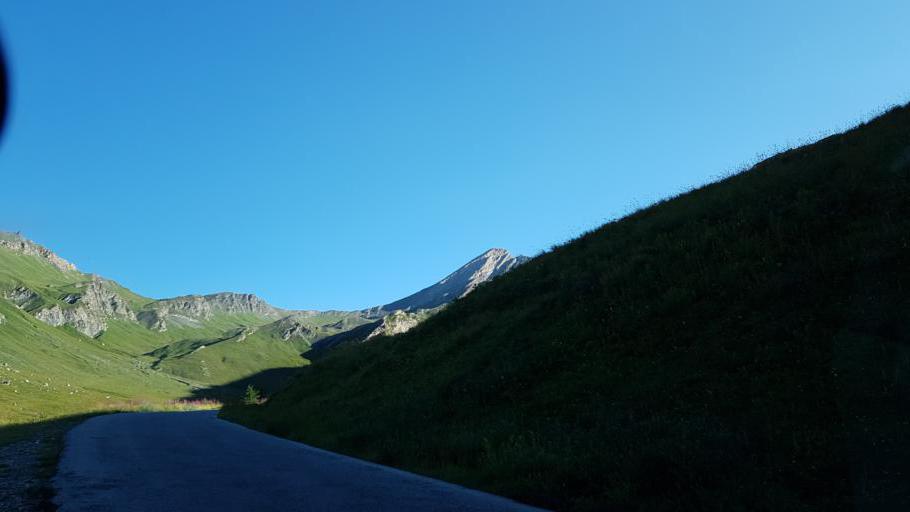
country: IT
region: Piedmont
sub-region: Provincia di Cuneo
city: Pontechianale
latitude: 44.6614
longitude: 6.9873
